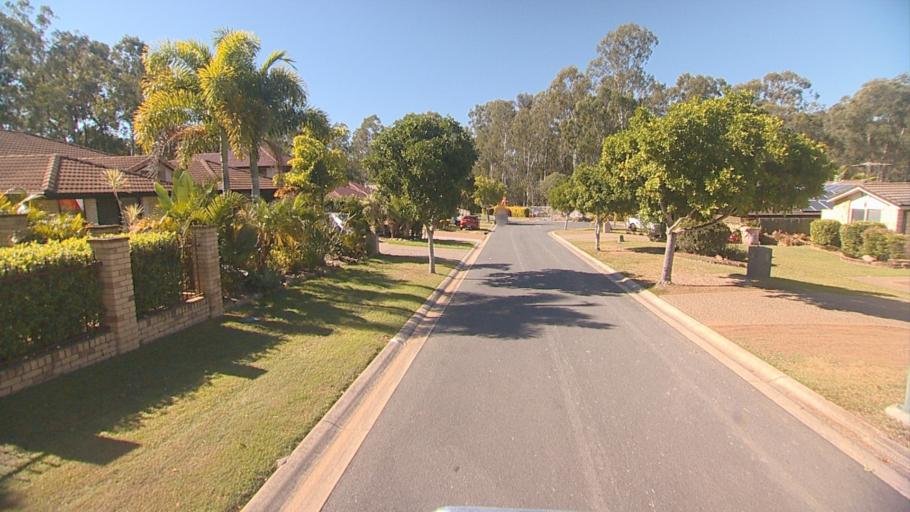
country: AU
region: Queensland
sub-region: Logan
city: Logan Reserve
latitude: -27.6889
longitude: 153.0643
